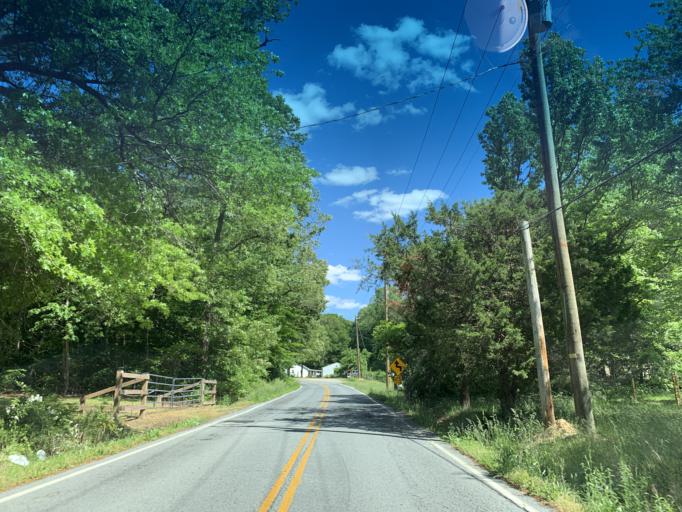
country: US
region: Maryland
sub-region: Cecil County
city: Elkton
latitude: 39.5937
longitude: -75.8632
